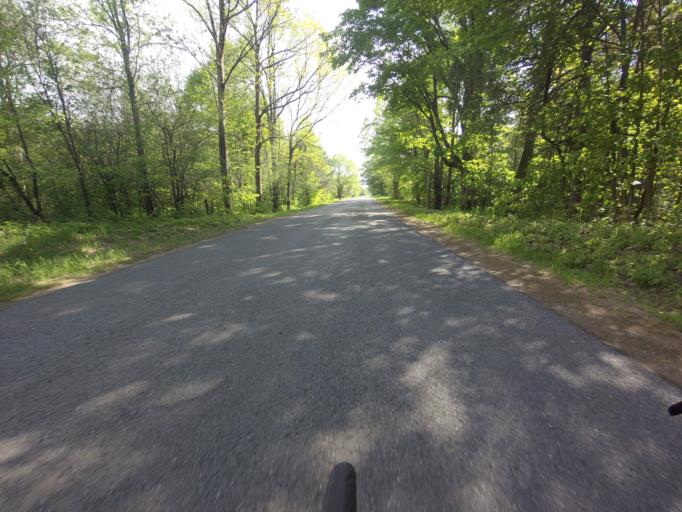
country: US
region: New York
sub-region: St. Lawrence County
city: Gouverneur
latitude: 44.2297
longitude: -75.2276
